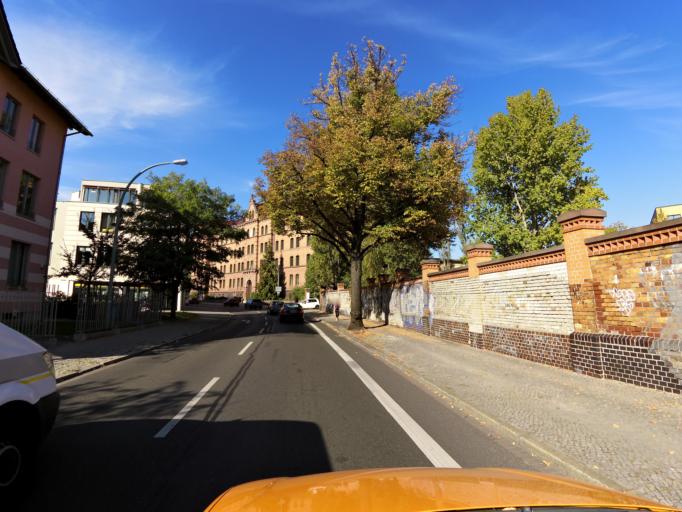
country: DE
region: Brandenburg
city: Potsdam
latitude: 52.4048
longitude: 13.0682
